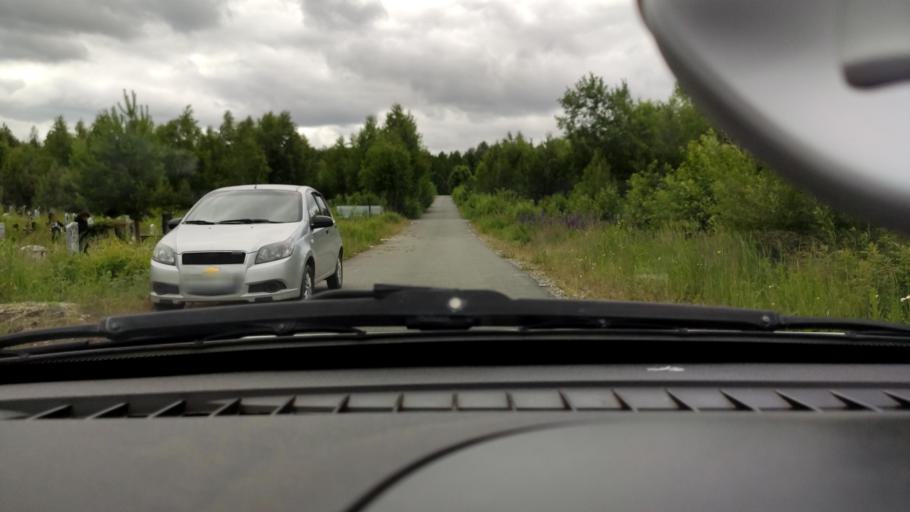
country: RU
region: Perm
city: Kondratovo
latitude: 58.0640
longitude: 56.1596
